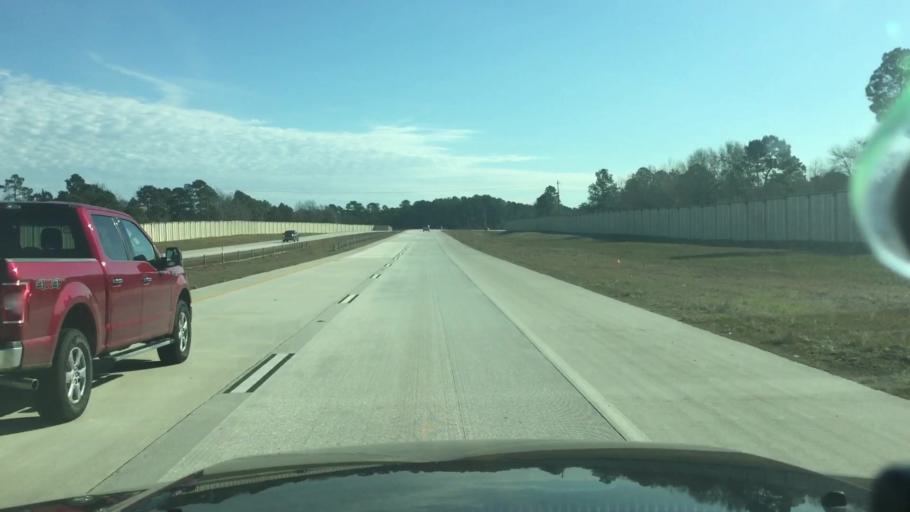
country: US
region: Texas
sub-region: Montgomery County
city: Porter Heights
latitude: 30.1375
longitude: -95.2634
